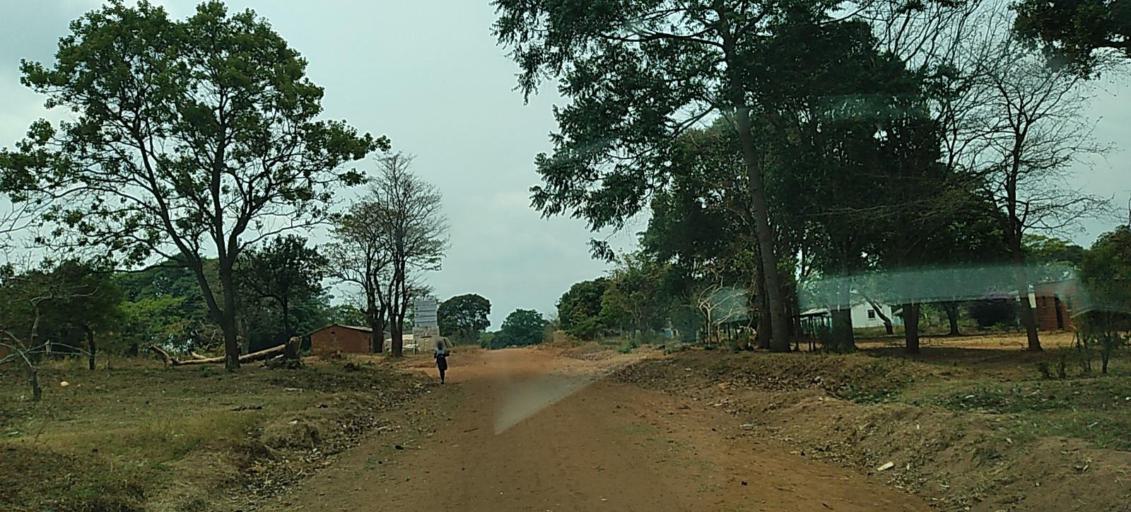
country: ZM
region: North-Western
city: Mwinilunga
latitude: -11.4404
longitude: 24.7471
